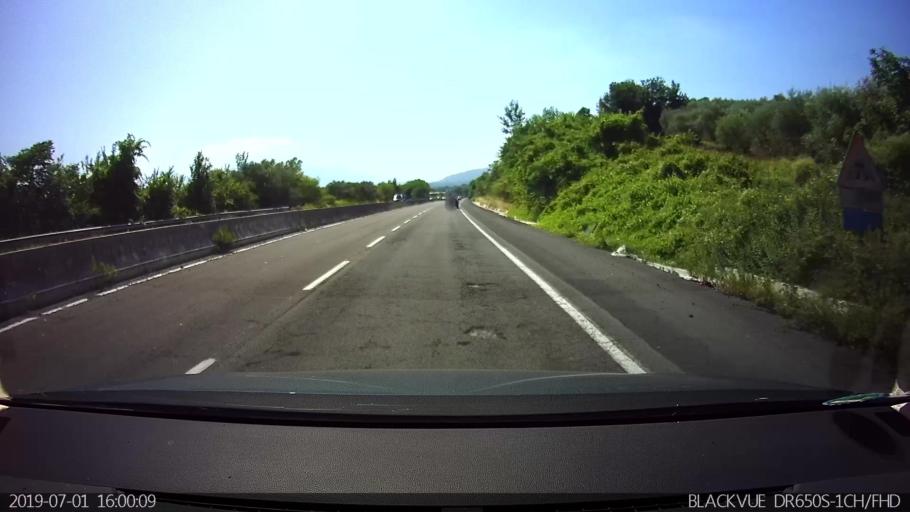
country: IT
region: Latium
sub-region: Provincia di Frosinone
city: San Giuseppe le Prata-Cotropagno
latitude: 41.6618
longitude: 13.4041
